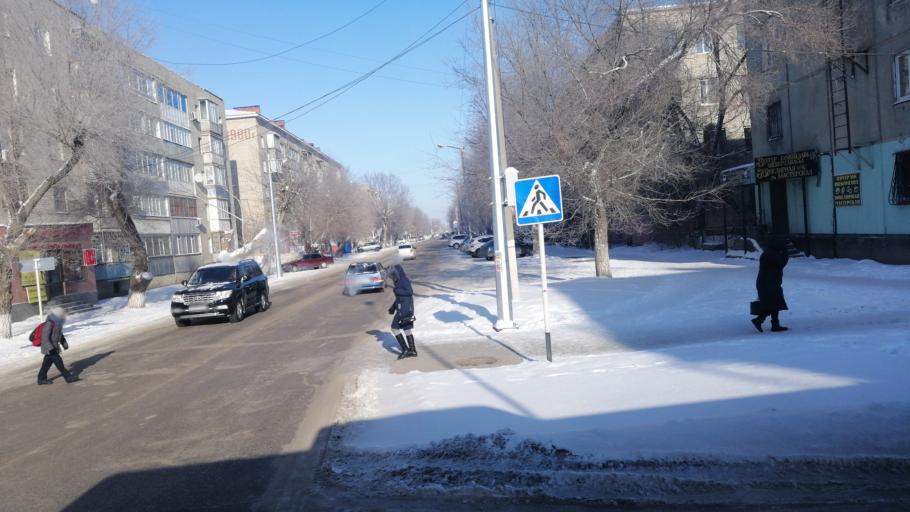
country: KZ
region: Aqtoebe
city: Aqtobe
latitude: 50.2816
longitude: 57.2203
